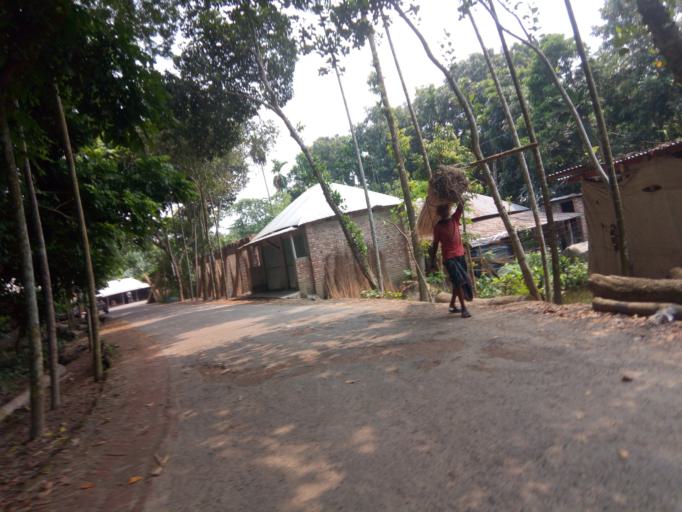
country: BD
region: Khulna
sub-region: Magura
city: Magura
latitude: 23.4477
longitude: 89.6240
